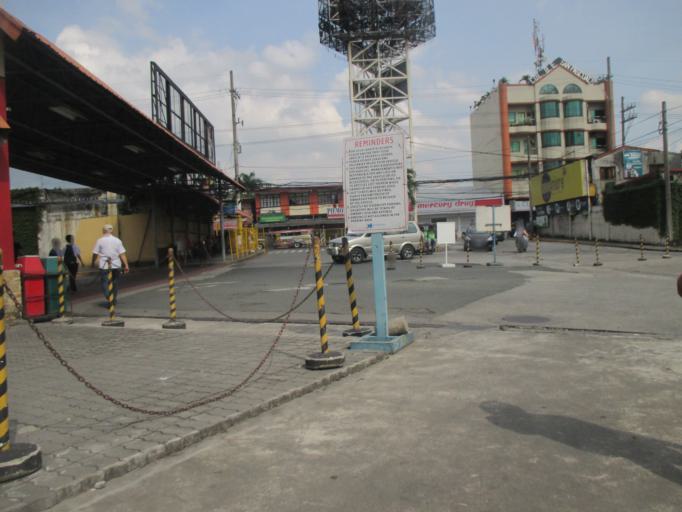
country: PH
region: Metro Manila
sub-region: Marikina
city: Calumpang
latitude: 14.6322
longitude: 121.0832
